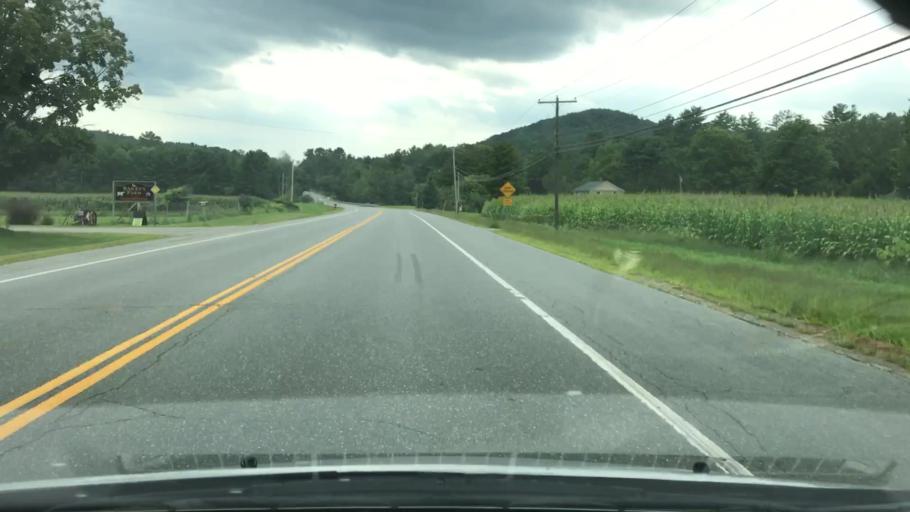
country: US
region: New Hampshire
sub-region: Grafton County
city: Lyme
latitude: 43.8052
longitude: -72.1647
